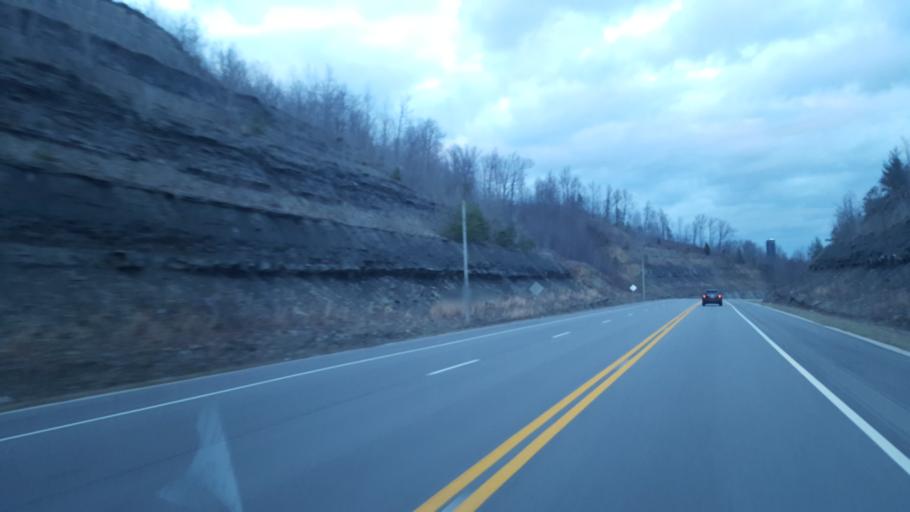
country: US
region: Kentucky
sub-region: Lewis County
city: Vanceburg
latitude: 38.5874
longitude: -83.2663
